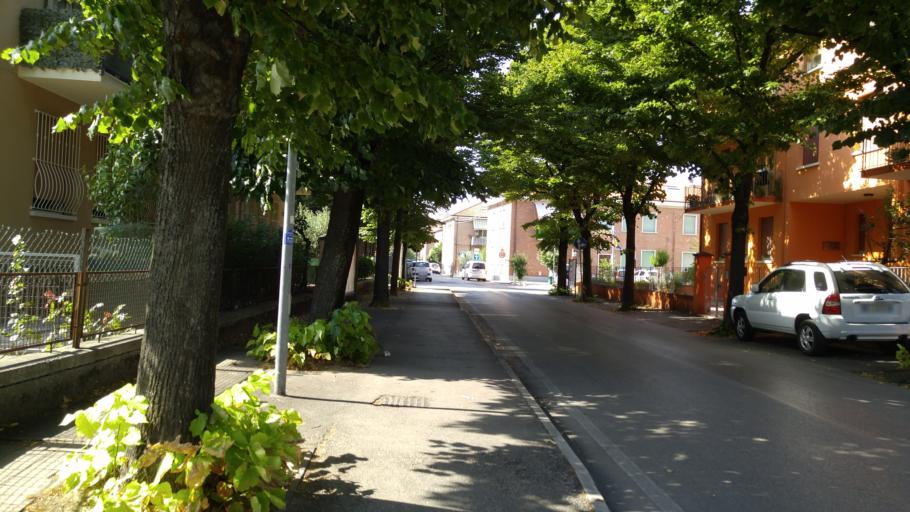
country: IT
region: The Marches
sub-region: Provincia di Pesaro e Urbino
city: Pesaro
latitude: 43.9011
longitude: 12.9206
